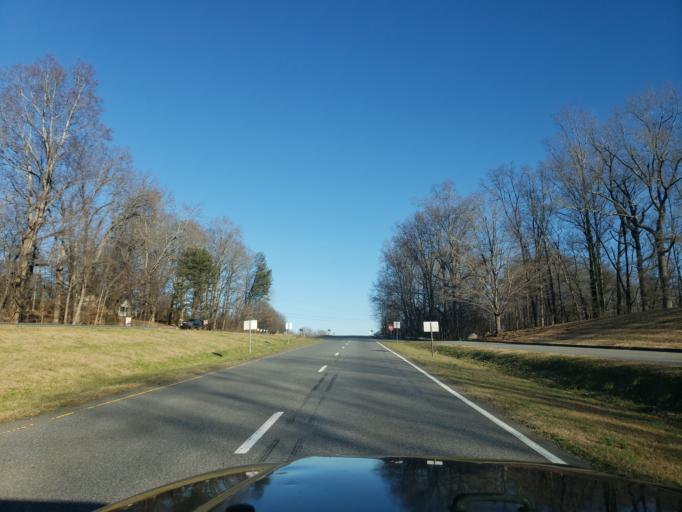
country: US
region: North Carolina
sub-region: Gaston County
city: Bessemer City
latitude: 35.2548
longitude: -81.2695
